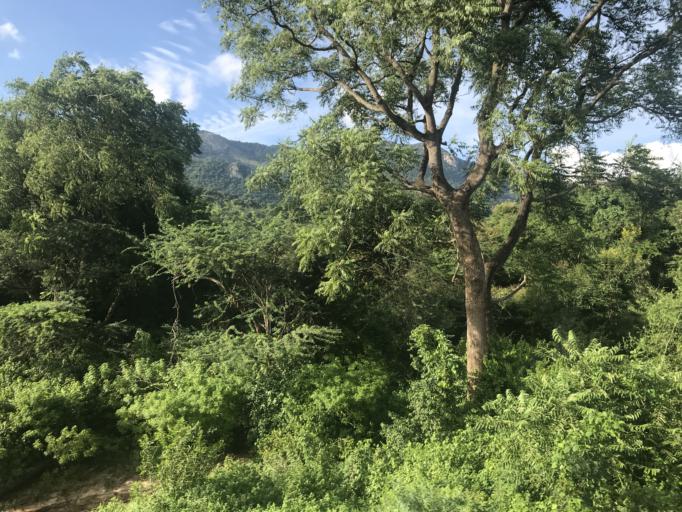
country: IN
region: Tamil Nadu
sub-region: Coimbatore
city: Madukkarai
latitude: 10.8763
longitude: 76.8558
